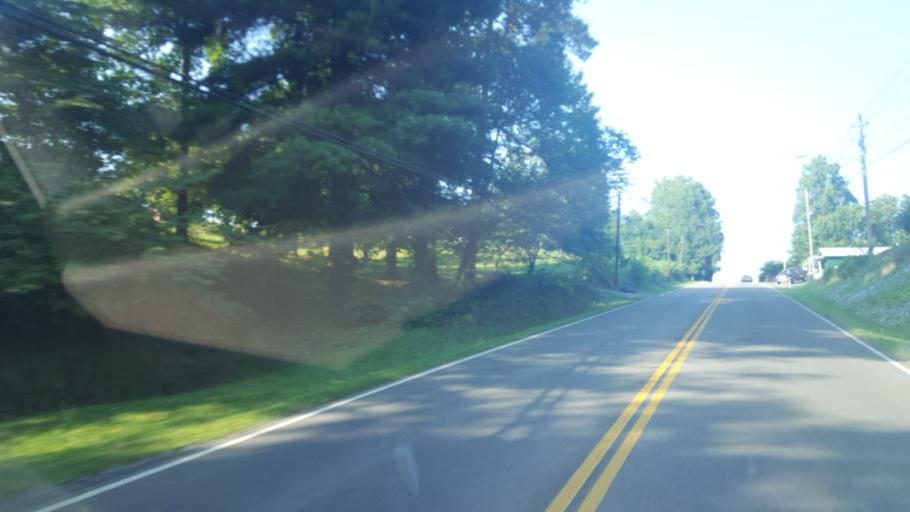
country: US
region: Tennessee
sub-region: Sullivan County
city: Bluff City
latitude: 36.4600
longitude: -82.2753
